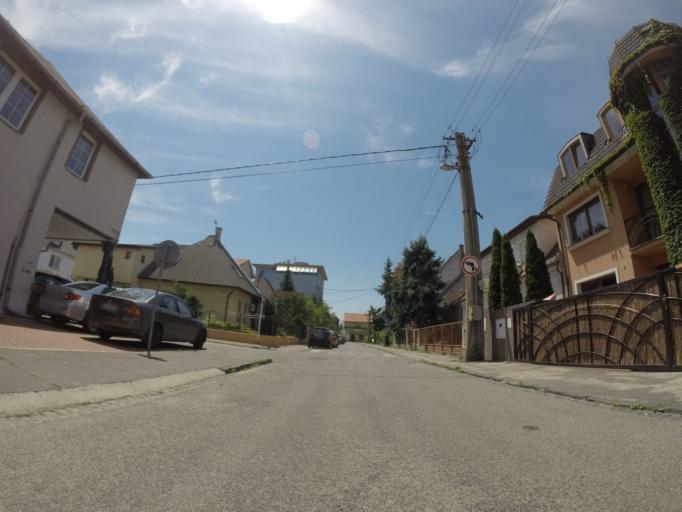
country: SK
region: Bratislavsky
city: Bratislava
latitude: 48.1721
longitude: 17.1354
